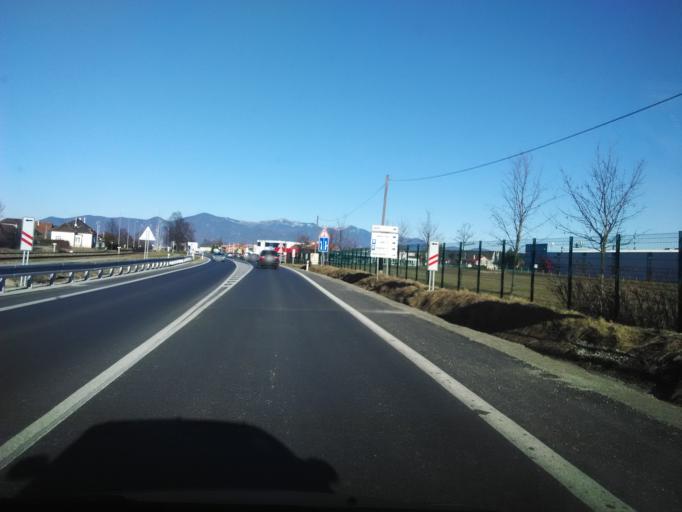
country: SK
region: Zilinsky
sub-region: Okres Martin
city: Martin
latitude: 49.0266
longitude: 18.9054
